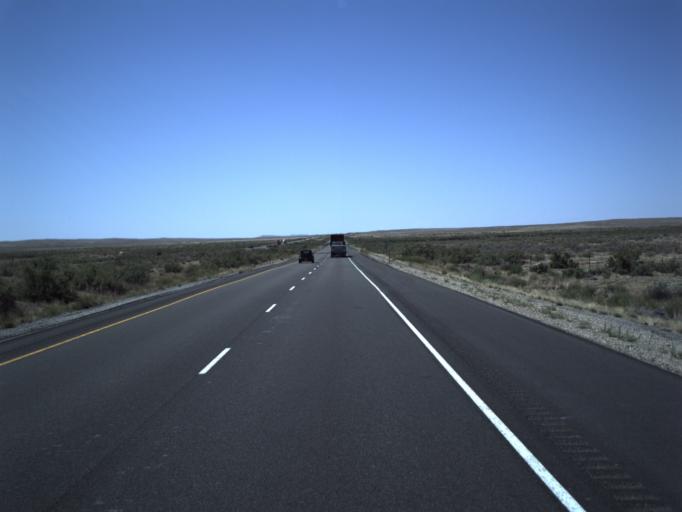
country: US
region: Colorado
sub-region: Mesa County
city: Loma
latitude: 39.0855
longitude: -109.2207
